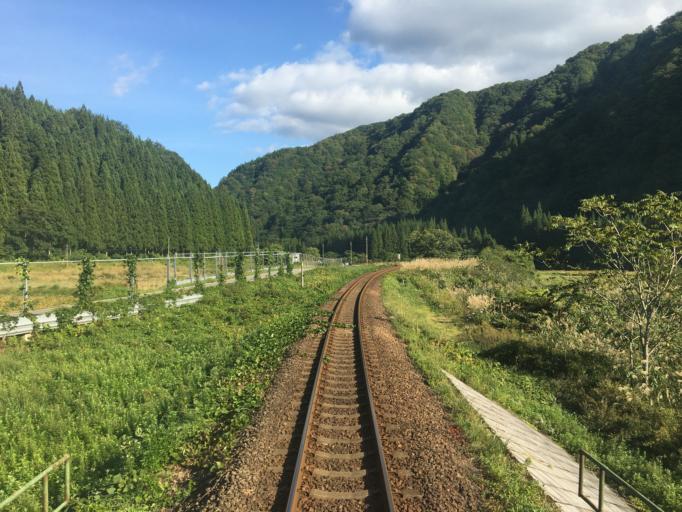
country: JP
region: Akita
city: Kakunodatemachi
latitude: 39.9184
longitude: 140.5197
